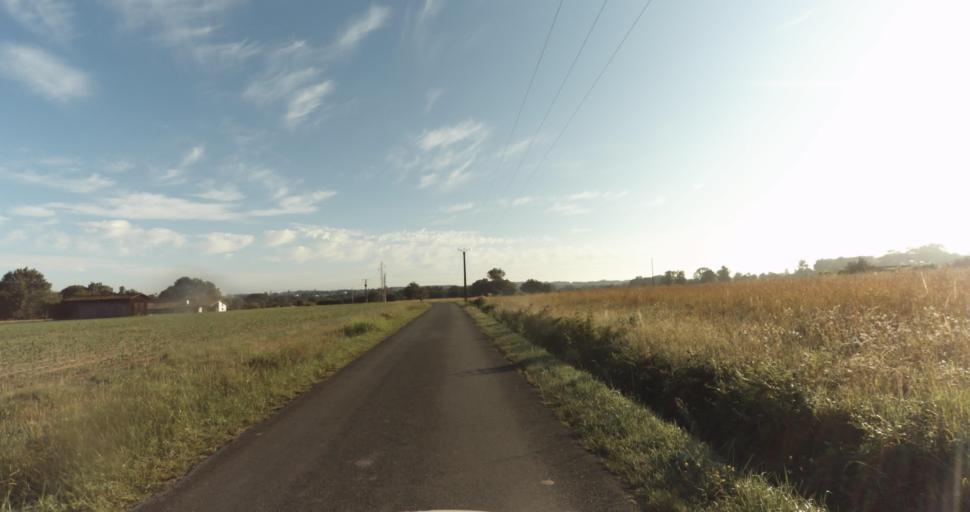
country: FR
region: Aquitaine
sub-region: Departement de la Gironde
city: Bazas
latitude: 44.4217
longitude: -0.2329
